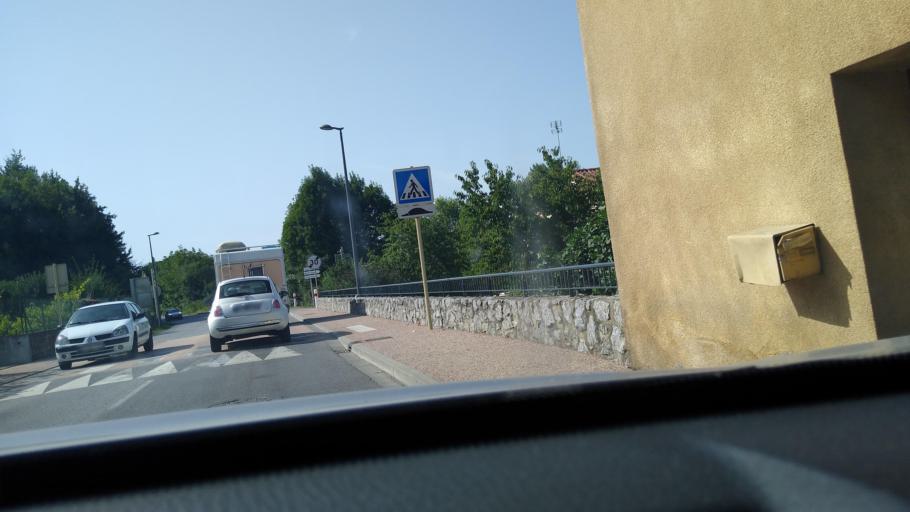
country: FR
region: Midi-Pyrenees
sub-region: Departement de l'Ariege
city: Saint-Lizier
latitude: 43.0309
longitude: 1.0835
